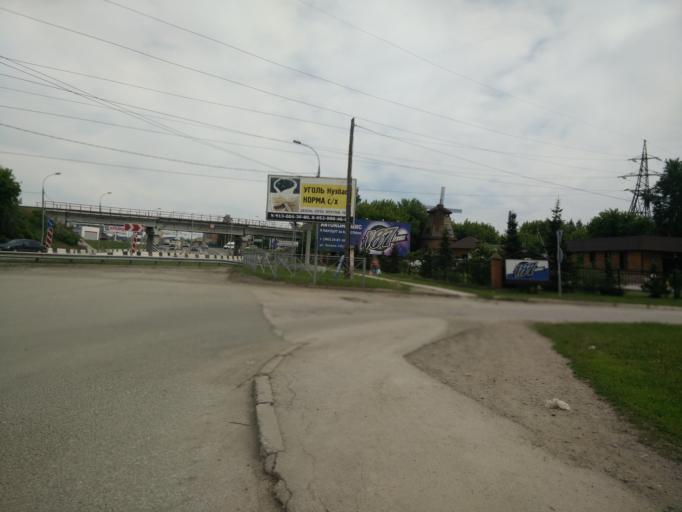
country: RU
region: Novosibirsk
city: Berdsk
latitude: 54.7541
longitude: 83.1251
